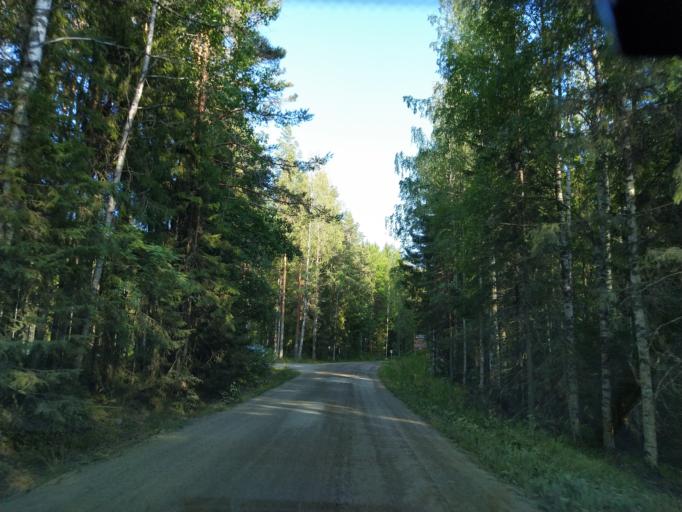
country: FI
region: Central Finland
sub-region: Jaemsae
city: Kuhmoinen
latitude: 61.6755
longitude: 24.9967
